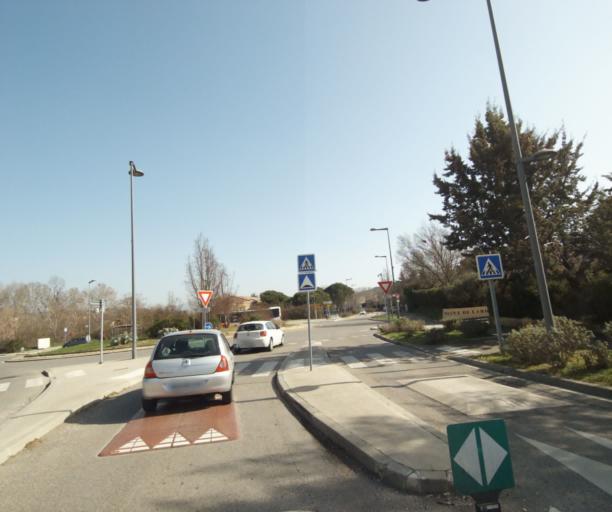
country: FR
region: Provence-Alpes-Cote d'Azur
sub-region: Departement des Bouches-du-Rhone
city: Aix-en-Provence
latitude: 43.5099
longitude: 5.4354
